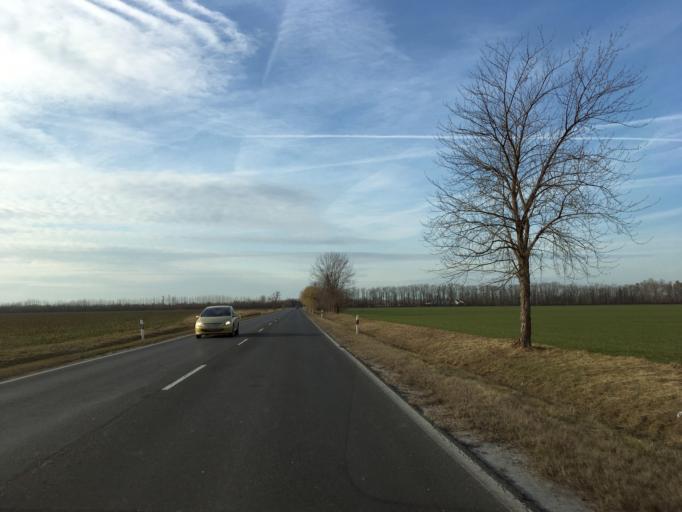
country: HU
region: Gyor-Moson-Sopron
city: Otteveny
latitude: 47.7137
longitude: 17.5141
